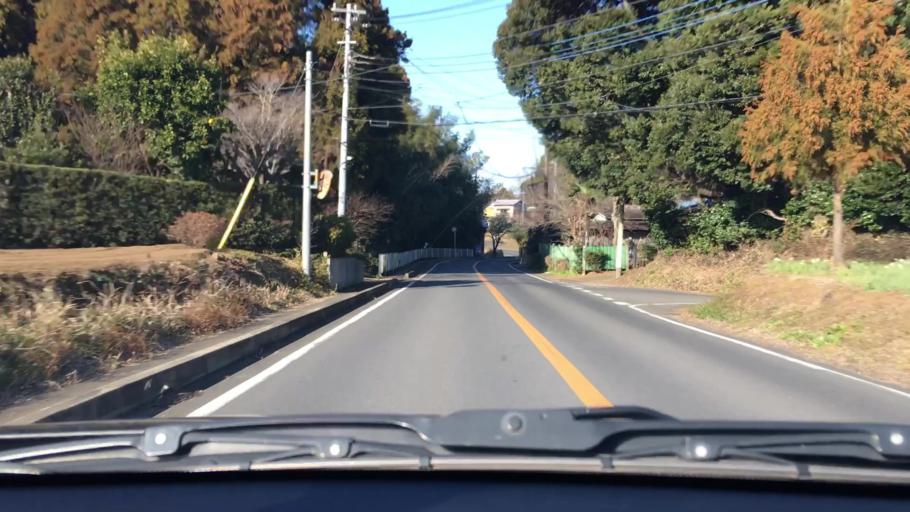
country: JP
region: Chiba
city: Shisui
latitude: 35.6987
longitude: 140.2534
